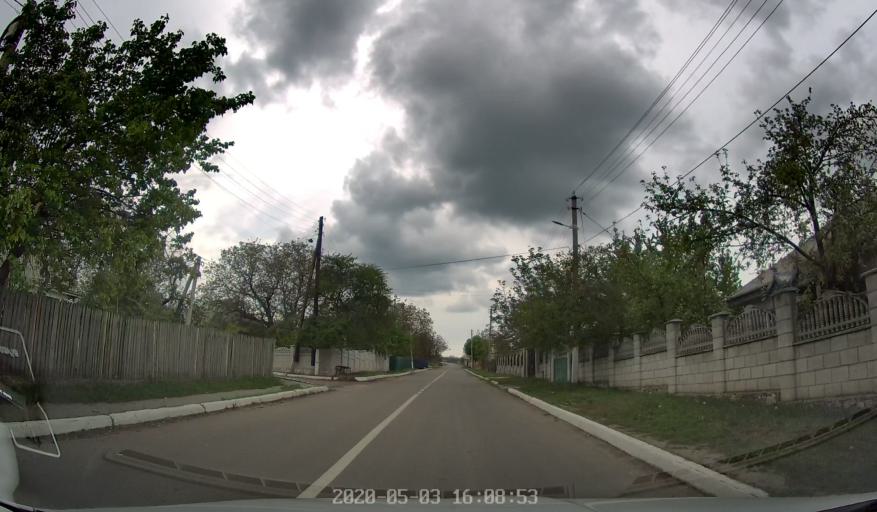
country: MD
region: Calarasi
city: Calarasi
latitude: 47.1978
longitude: 28.3424
